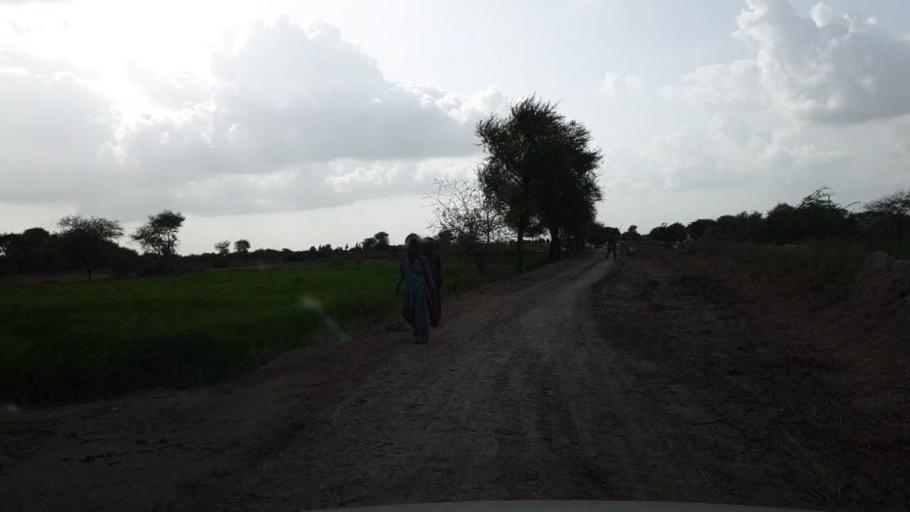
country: PK
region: Sindh
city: Kario
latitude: 24.7633
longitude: 68.6027
